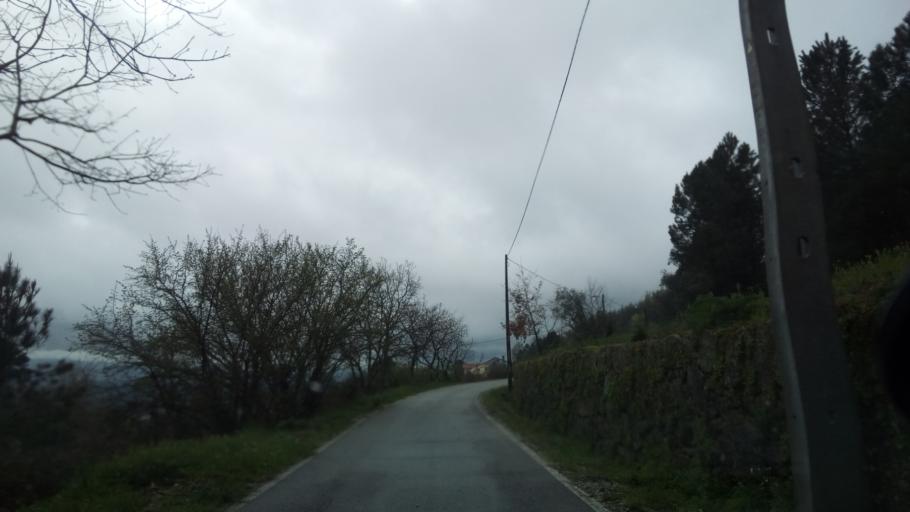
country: PT
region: Guarda
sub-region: Fornos de Algodres
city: Fornos de Algodres
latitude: 40.6299
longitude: -7.5286
